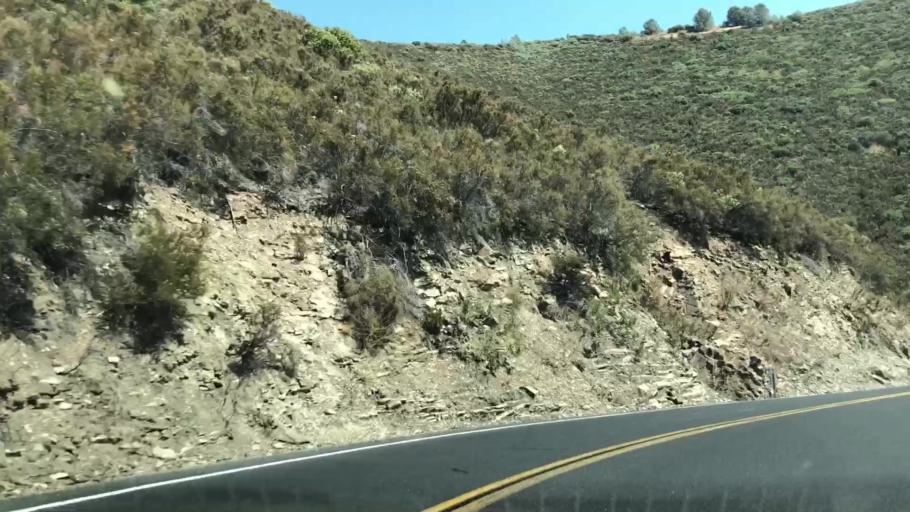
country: US
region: California
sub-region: Tuolumne County
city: Tuolumne City
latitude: 37.8226
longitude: -120.2763
